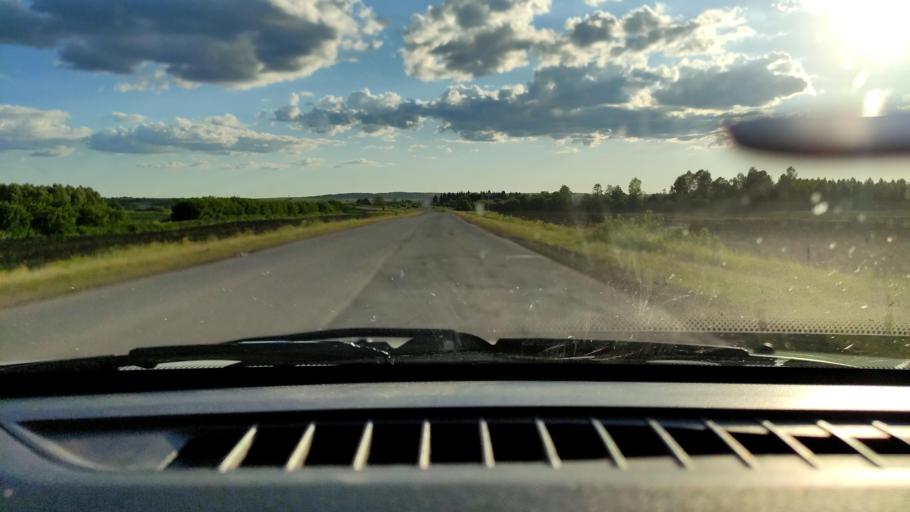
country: RU
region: Perm
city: Uinskoye
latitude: 57.0761
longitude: 56.6043
